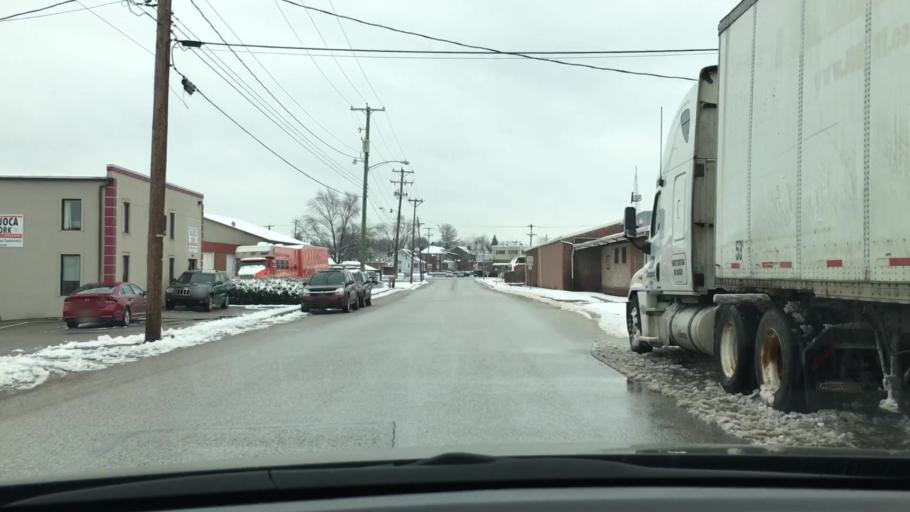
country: US
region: Pennsylvania
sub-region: York County
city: Valley View
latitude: 39.9590
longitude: -76.7052
